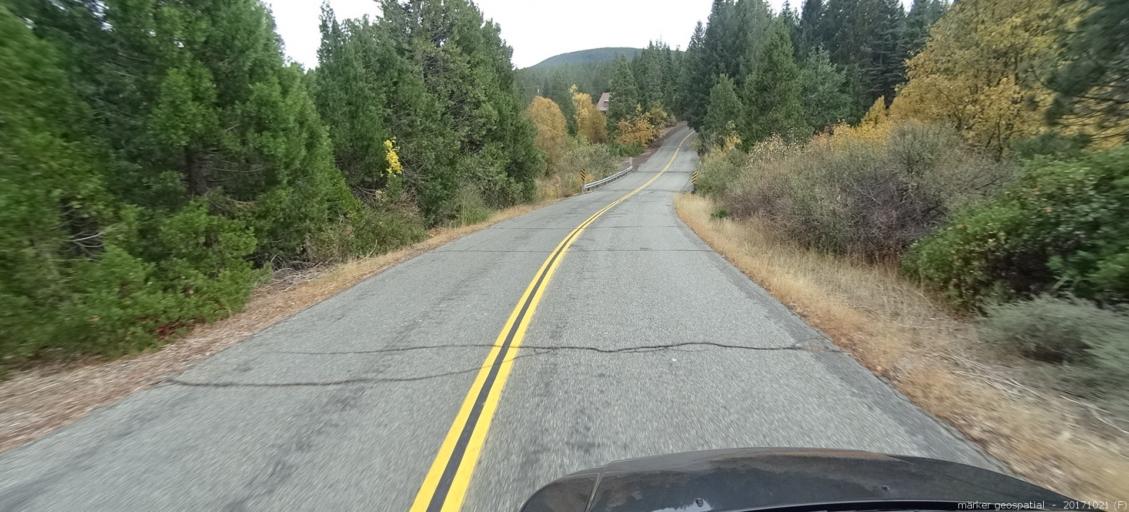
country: US
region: California
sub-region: Shasta County
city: Burney
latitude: 40.8611
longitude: -121.8473
